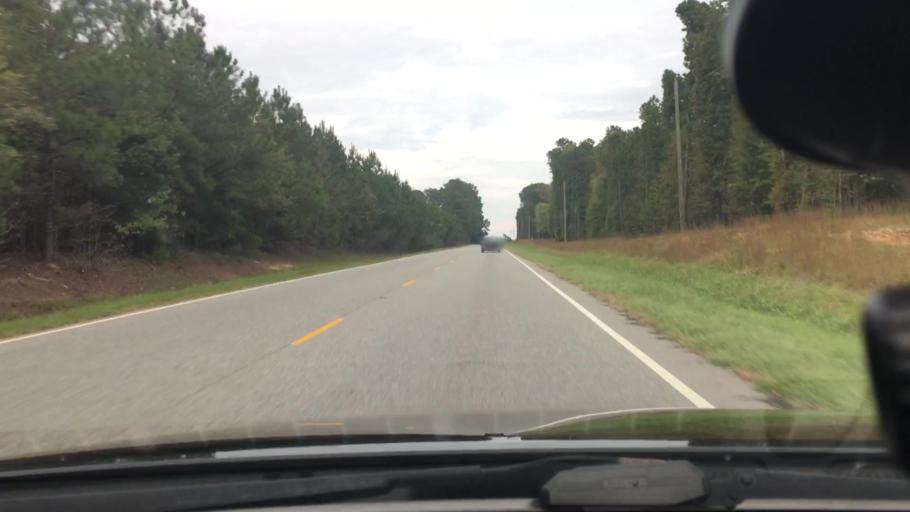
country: US
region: North Carolina
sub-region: Montgomery County
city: Biscoe
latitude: 35.3701
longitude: -79.6753
